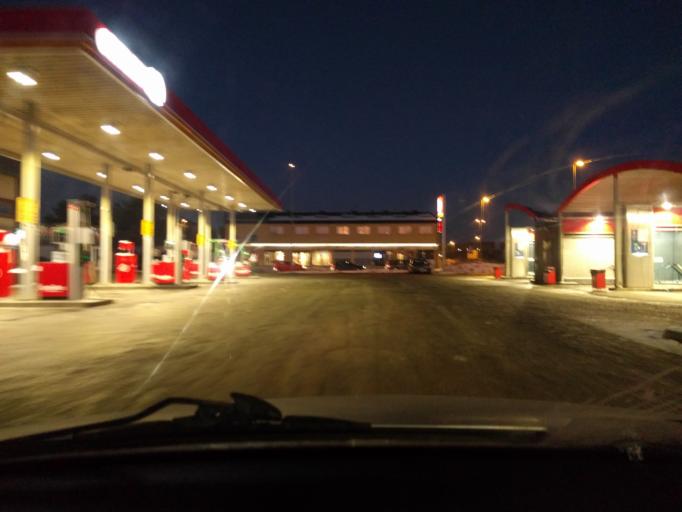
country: NO
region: Hedmark
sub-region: Hamar
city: Hamar
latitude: 60.7972
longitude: 11.0870
